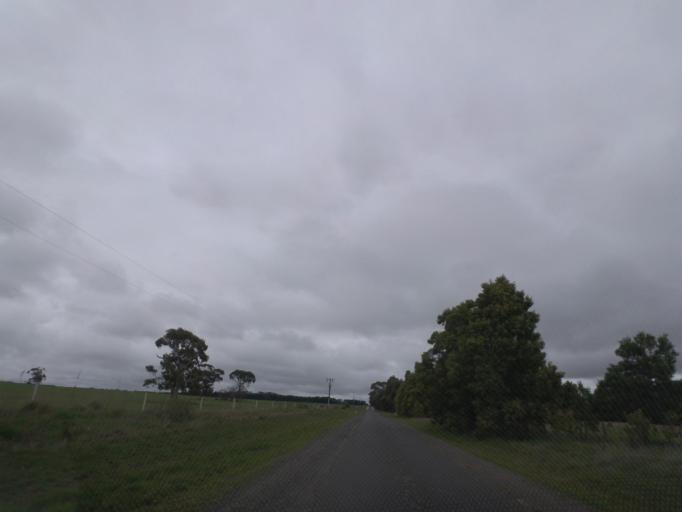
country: AU
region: Victoria
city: Brown Hill
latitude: -37.6257
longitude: 144.0516
